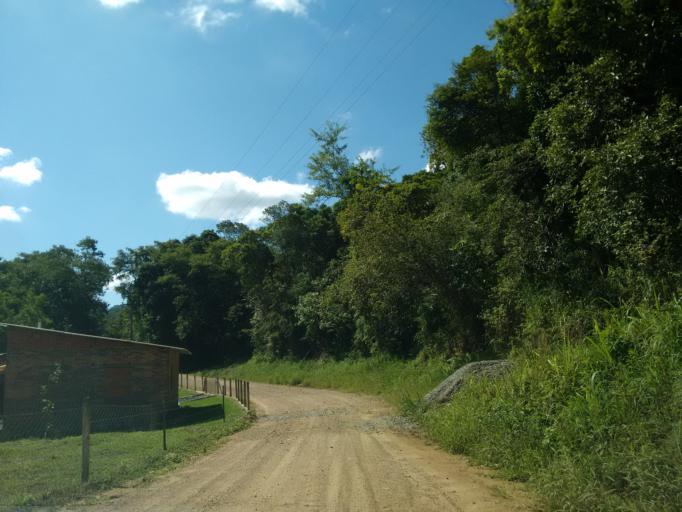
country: BR
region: Santa Catarina
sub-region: Indaial
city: Indaial
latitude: -26.9447
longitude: -49.1805
